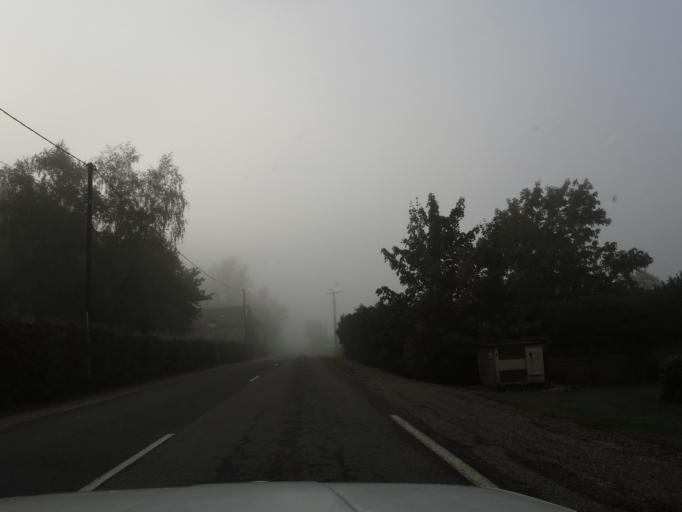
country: FR
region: Rhone-Alpes
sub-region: Departement de l'Isere
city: Bouvesse-Quirieu
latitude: 45.7915
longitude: 5.4617
